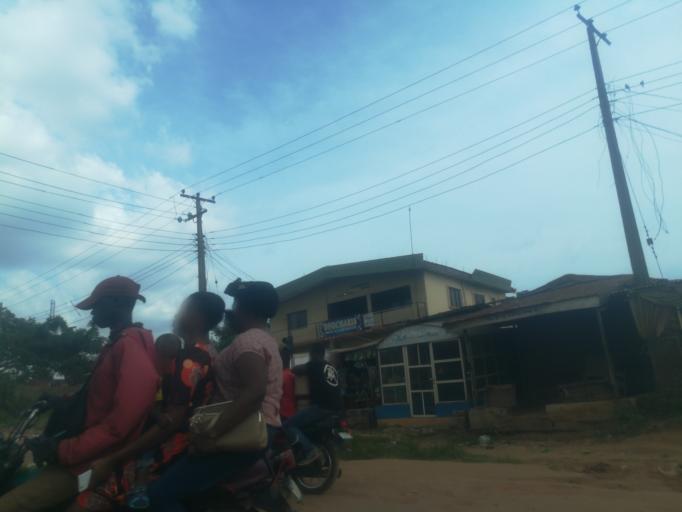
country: NG
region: Ogun
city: Abeokuta
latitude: 7.1242
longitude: 3.3230
